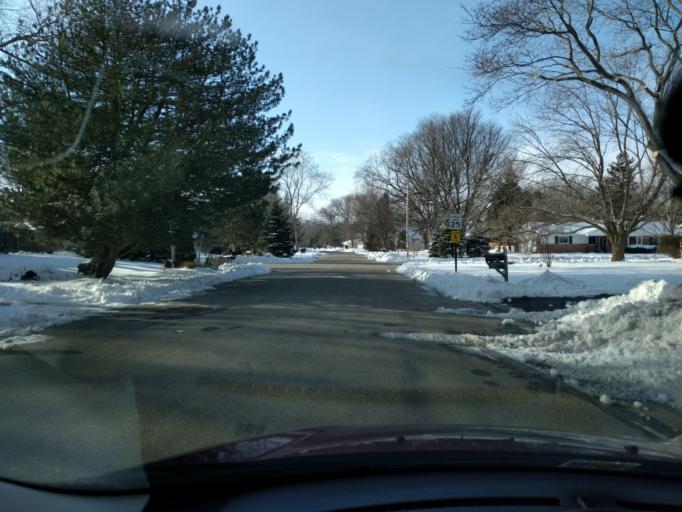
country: US
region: Wisconsin
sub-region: Milwaukee County
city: Glendale
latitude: 43.1262
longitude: -87.9186
